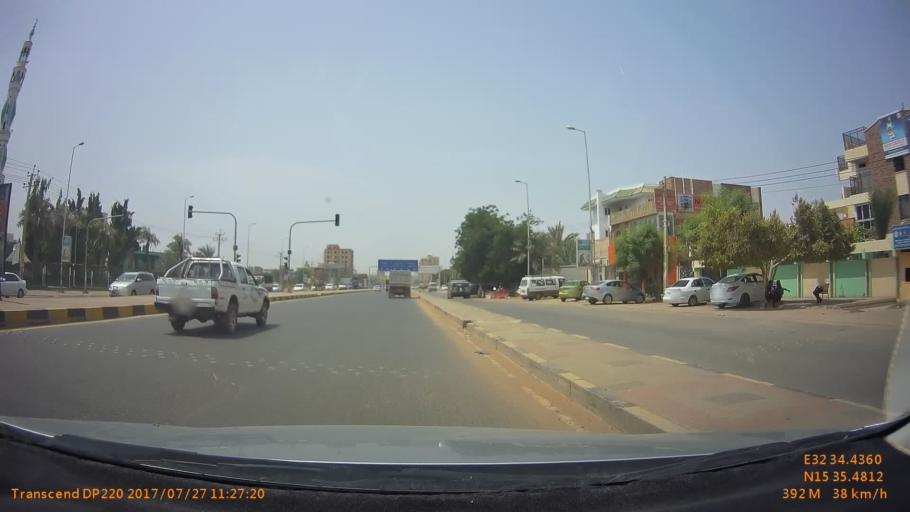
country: SD
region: Khartoum
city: Khartoum
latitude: 15.5913
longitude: 32.5739
